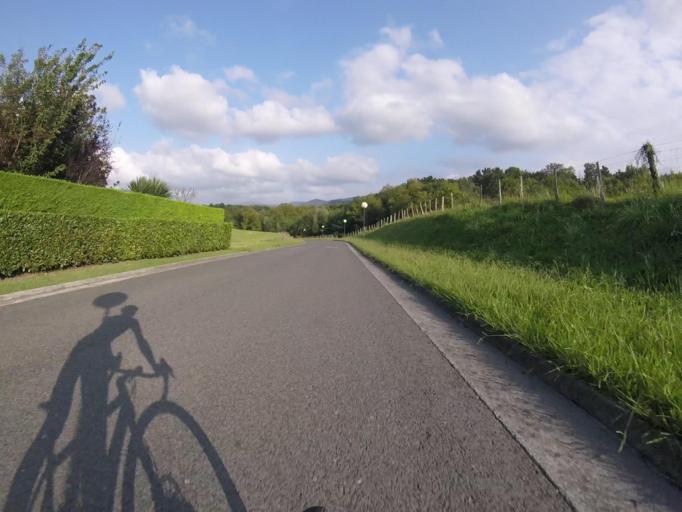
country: ES
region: Basque Country
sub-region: Provincia de Guipuzcoa
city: Irun
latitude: 43.3349
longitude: -1.8343
